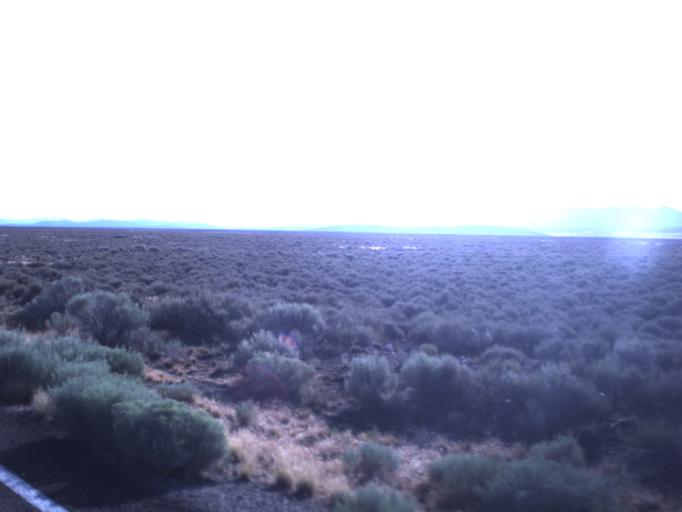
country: US
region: Utah
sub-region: Iron County
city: Enoch
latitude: 37.9404
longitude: -113.0222
